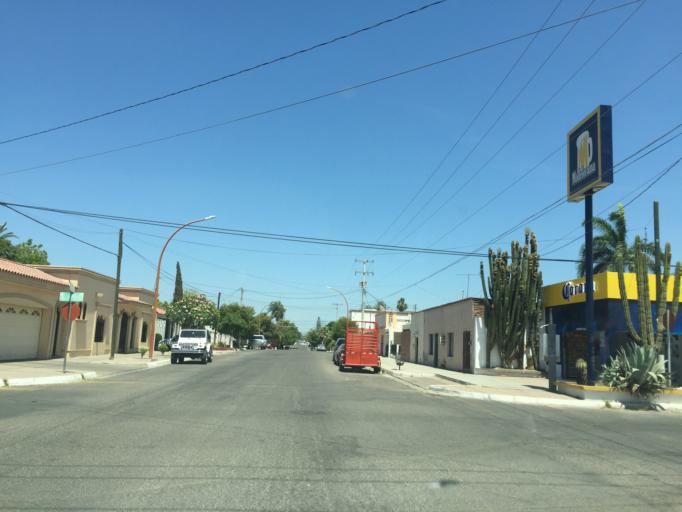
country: MX
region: Sonora
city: Navojoa
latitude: 27.0829
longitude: -109.4527
